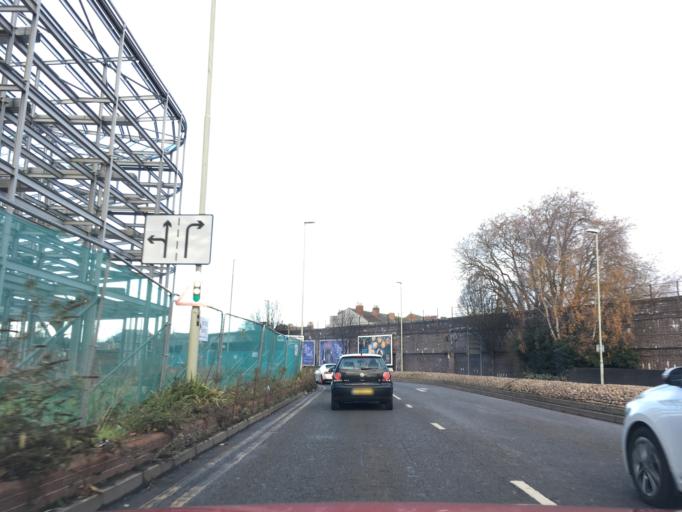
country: GB
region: England
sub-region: Gloucestershire
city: Gloucester
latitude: 51.8678
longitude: -2.2417
